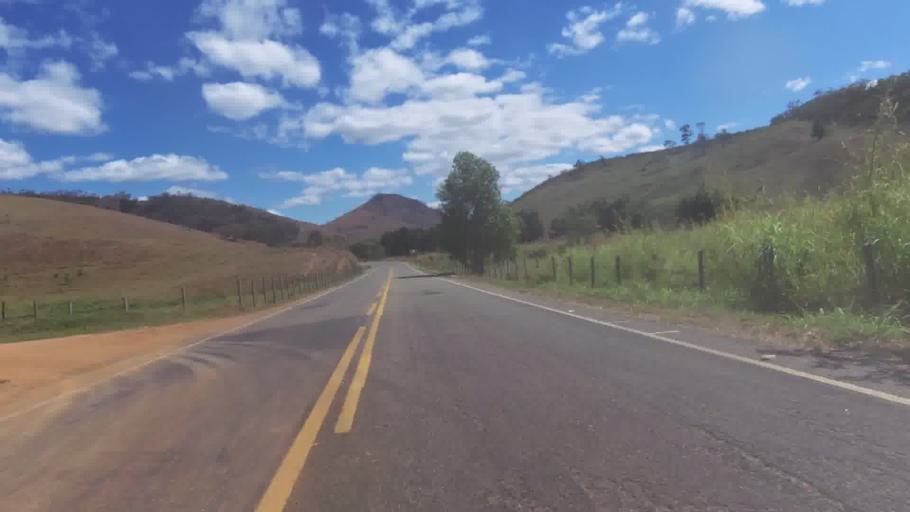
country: BR
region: Espirito Santo
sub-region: Cachoeiro De Itapemirim
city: Cachoeiro de Itapemirim
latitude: -20.9151
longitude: -41.2339
